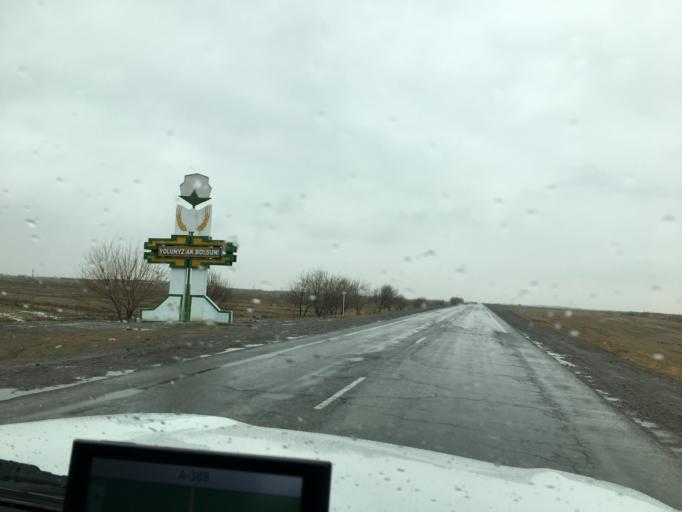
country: TM
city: Murgab
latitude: 37.4459
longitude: 62.0846
